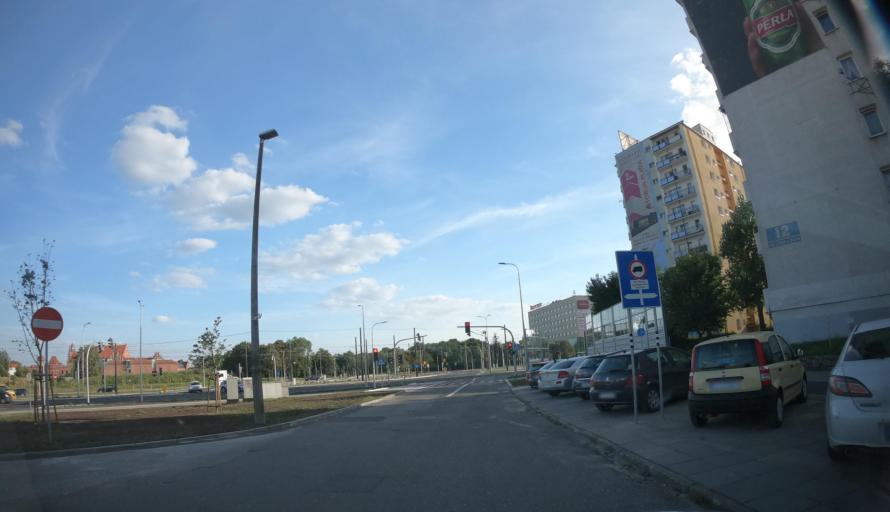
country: PL
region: Kujawsko-Pomorskie
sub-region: Torun
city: Torun
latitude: 53.0149
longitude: 18.5986
